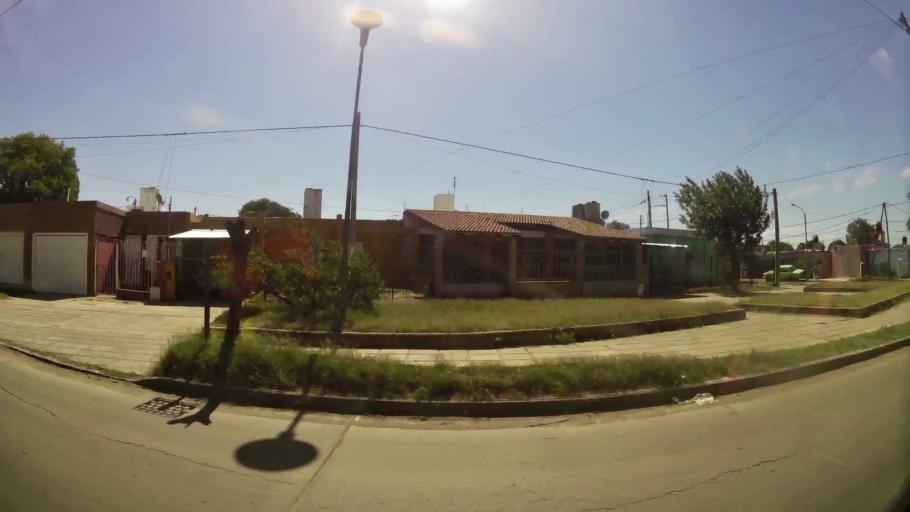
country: AR
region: Cordoba
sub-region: Departamento de Capital
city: Cordoba
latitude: -31.3717
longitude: -64.1556
